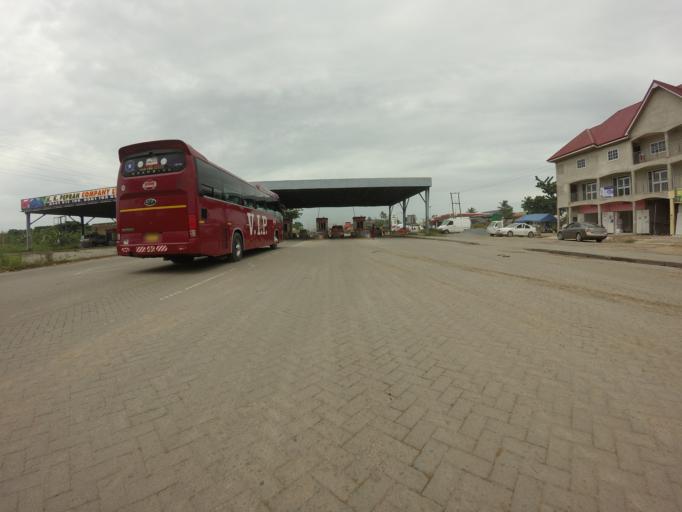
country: GH
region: Greater Accra
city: Achiaman
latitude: 5.7339
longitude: -0.3135
